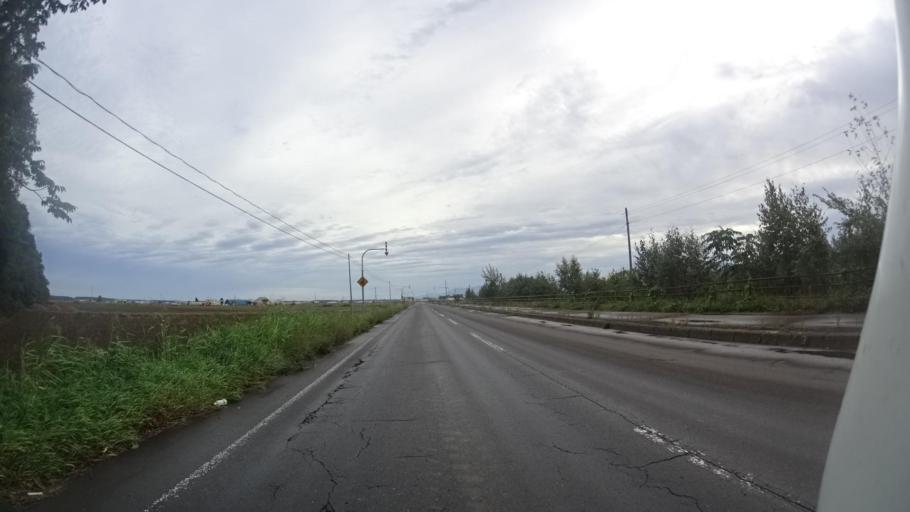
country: JP
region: Hokkaido
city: Abashiri
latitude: 43.8630
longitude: 144.6193
